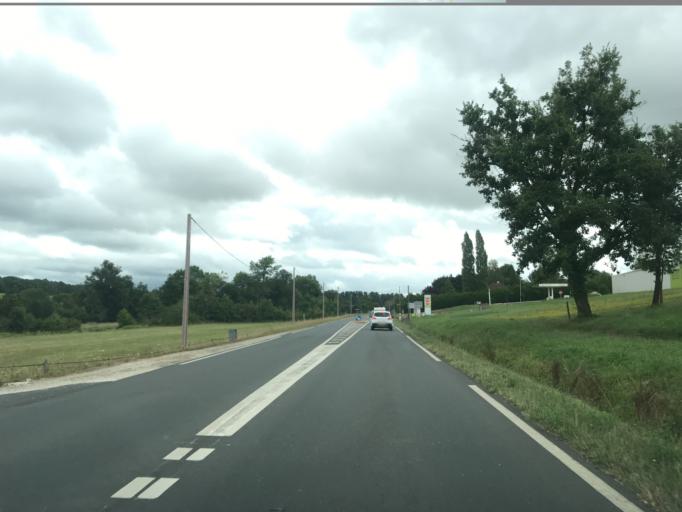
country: FR
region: Aquitaine
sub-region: Departement de la Dordogne
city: Mareuil
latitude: 45.4477
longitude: 0.4656
